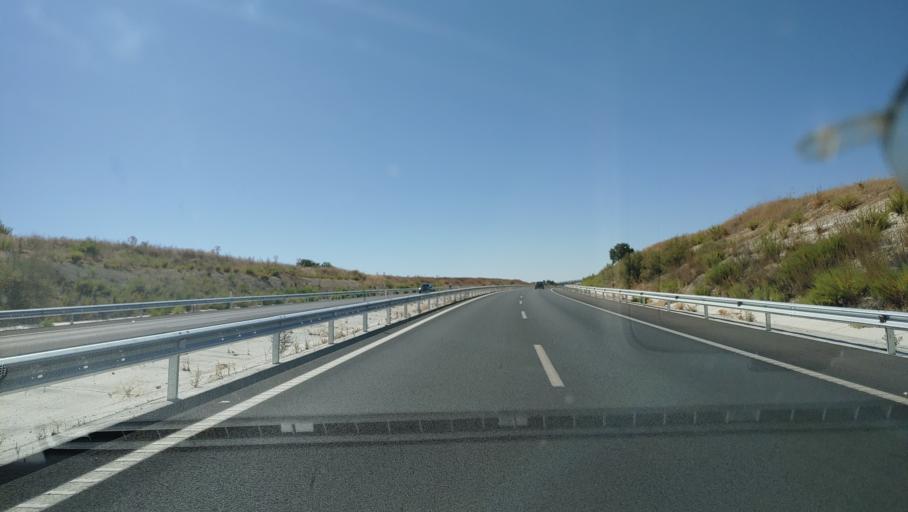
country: ES
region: Andalusia
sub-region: Provincia de Jaen
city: Torreperogil
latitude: 38.0414
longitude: -3.2666
